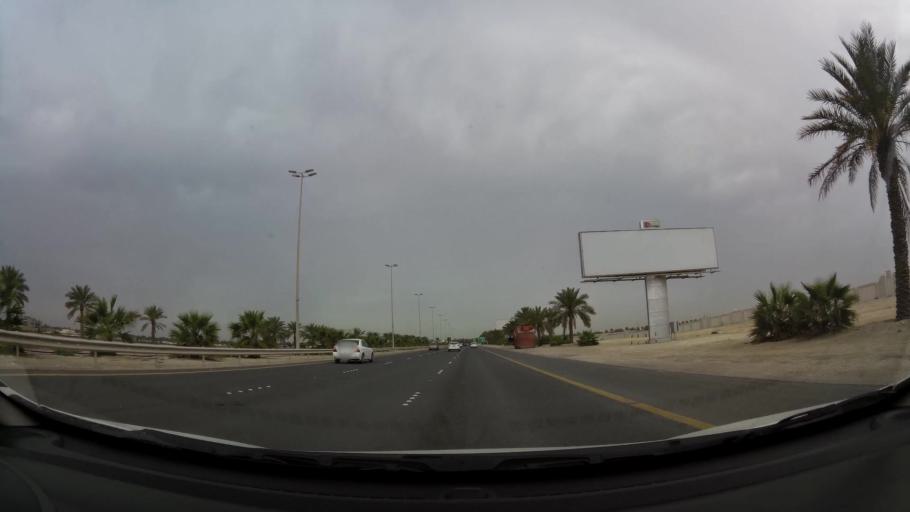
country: BH
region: Central Governorate
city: Dar Kulayb
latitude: 26.0506
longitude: 50.5000
